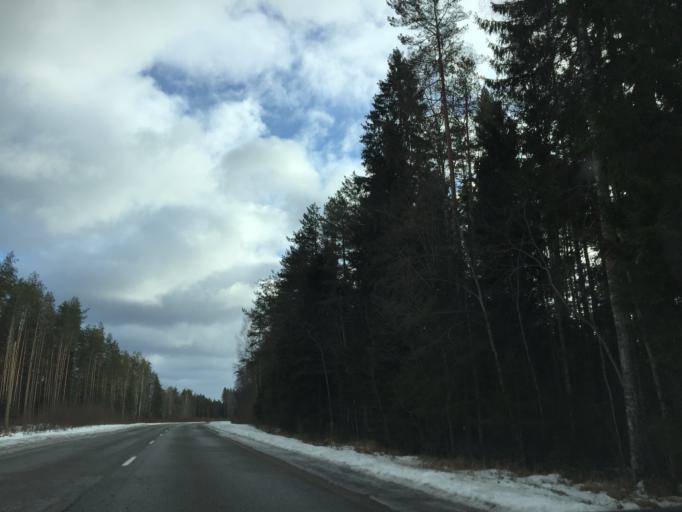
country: LV
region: Aloja
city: Staicele
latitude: 57.8599
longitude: 24.7013
